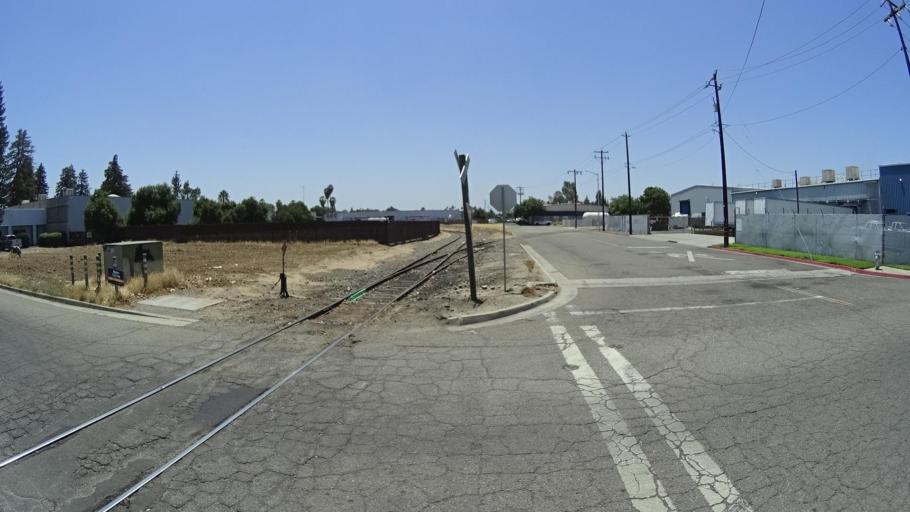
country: US
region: California
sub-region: Fresno County
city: Sunnyside
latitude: 36.7632
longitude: -119.7094
